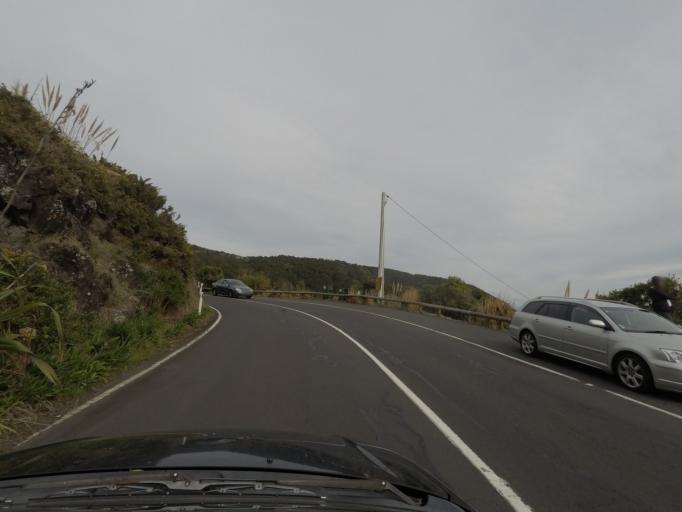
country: NZ
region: Auckland
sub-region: Auckland
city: Muriwai Beach
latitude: -36.9624
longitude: 174.4738
